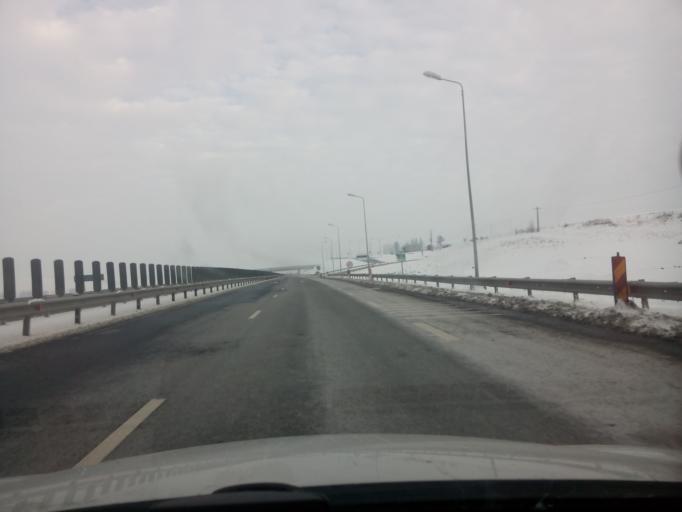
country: RO
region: Alba
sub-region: Comuna Cut
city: Cut
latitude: 45.9213
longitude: 23.6502
